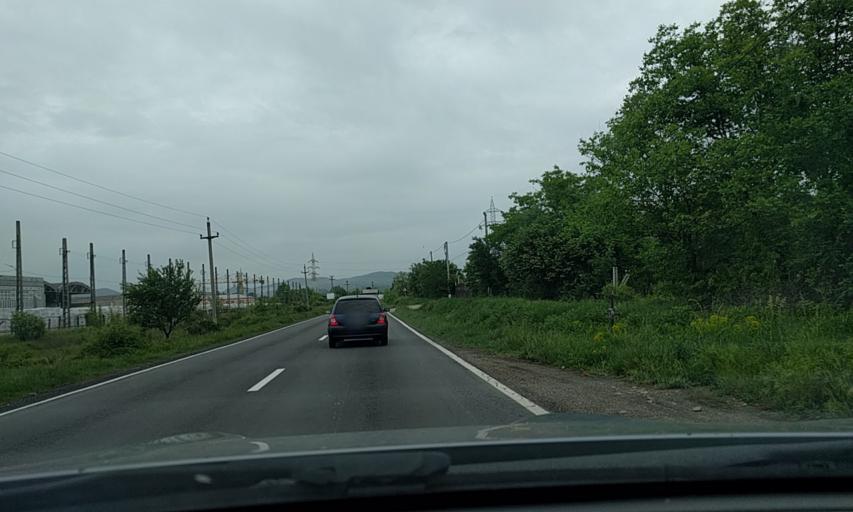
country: RO
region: Dambovita
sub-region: Comuna Vulcana-Pandele
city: Vulcana-Pandele
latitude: 45.0054
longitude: 25.4015
